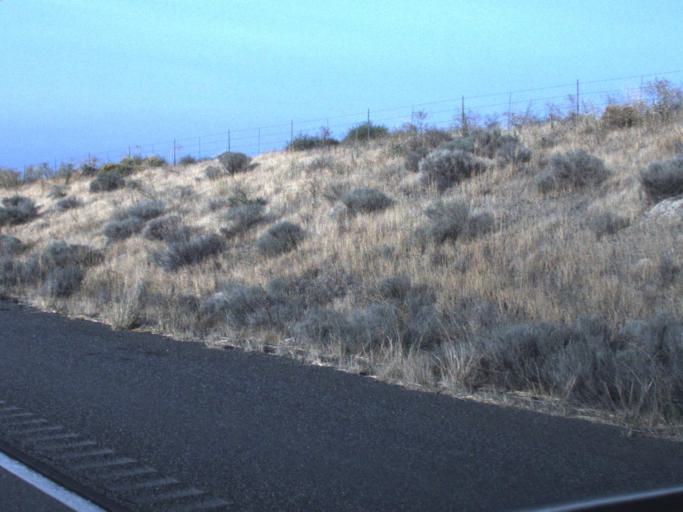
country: US
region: Washington
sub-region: Benton County
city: Highland
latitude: 46.0448
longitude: -119.2242
